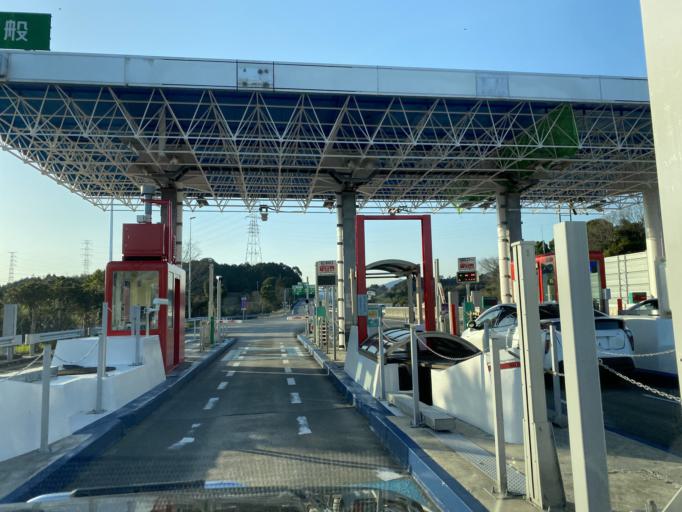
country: JP
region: Mie
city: Kameyama
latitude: 34.8387
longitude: 136.4198
